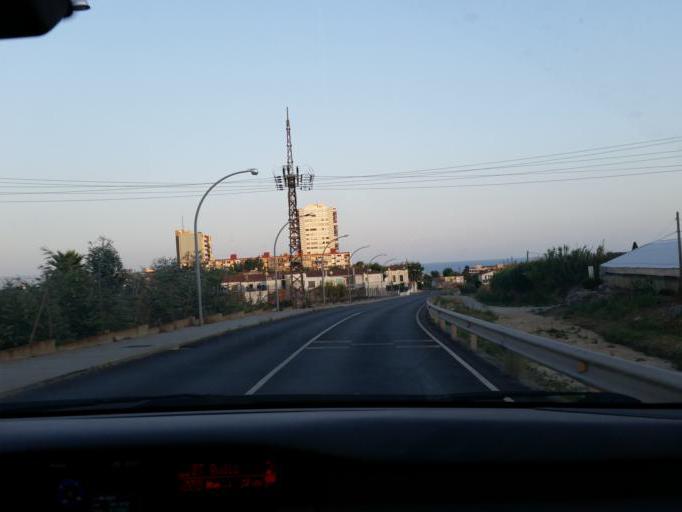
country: ES
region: Catalonia
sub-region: Provincia de Barcelona
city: Vilassar de Mar
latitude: 41.5099
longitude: 2.3836
